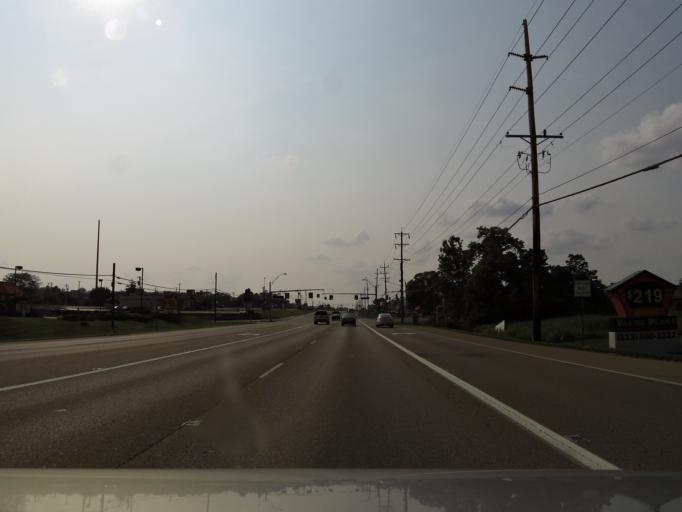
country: US
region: Ohio
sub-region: Hamilton County
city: Forest Park
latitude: 39.3180
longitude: -84.4940
